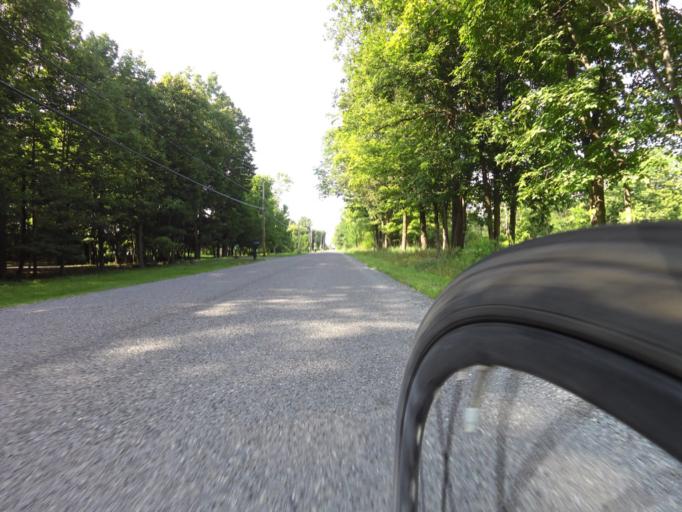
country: CA
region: Ontario
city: Kingston
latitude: 44.3767
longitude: -76.5952
